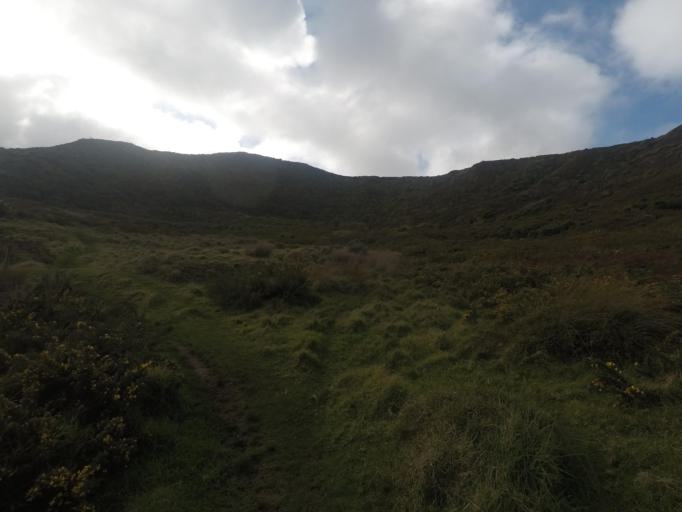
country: NZ
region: Auckland
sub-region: Auckland
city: Muriwai Beach
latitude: -36.8734
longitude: 174.4329
